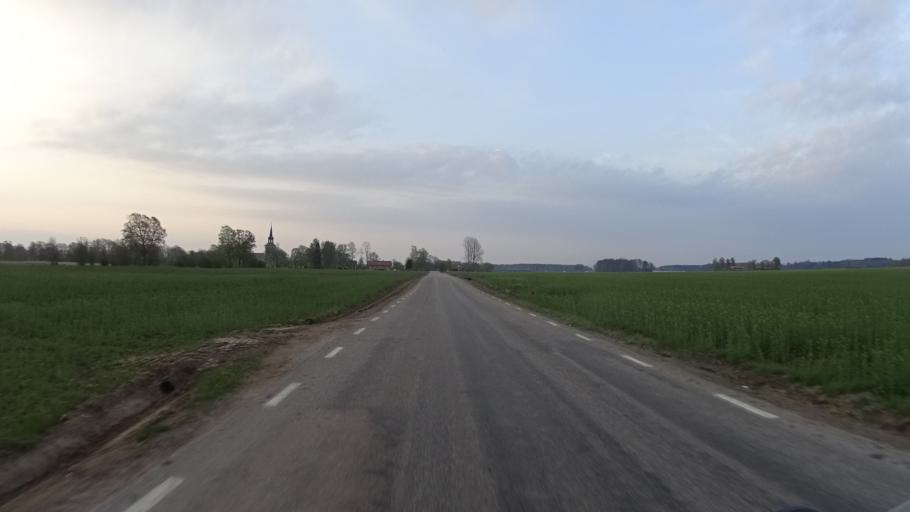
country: SE
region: Vaestra Goetaland
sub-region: Gotene Kommun
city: Kallby
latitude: 58.4764
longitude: 13.3228
